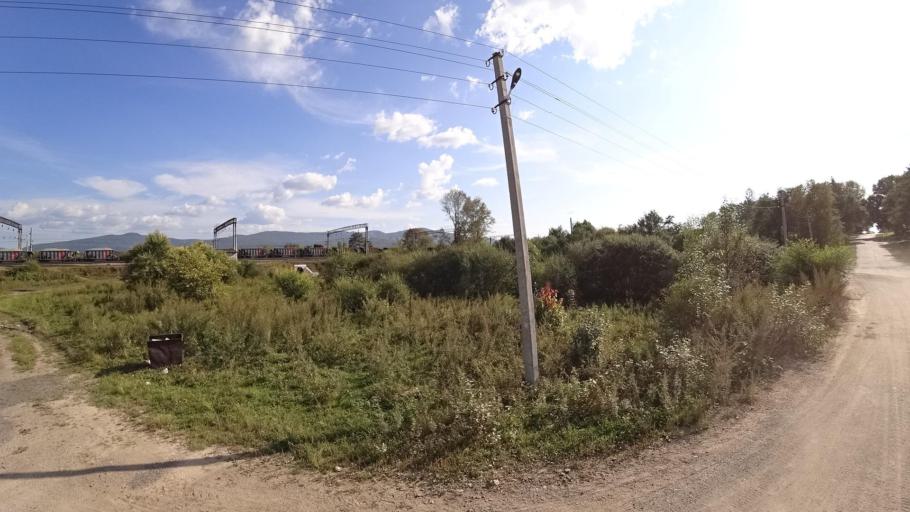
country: RU
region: Jewish Autonomous Oblast
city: Birakan
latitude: 48.9943
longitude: 131.7225
